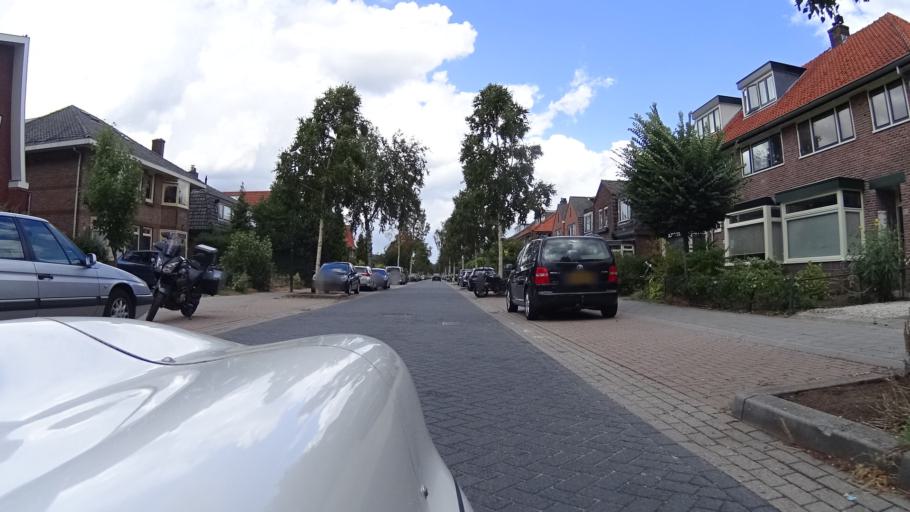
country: NL
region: Utrecht
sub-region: Gemeente De Bilt
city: De Bilt
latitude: 52.1104
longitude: 5.1778
